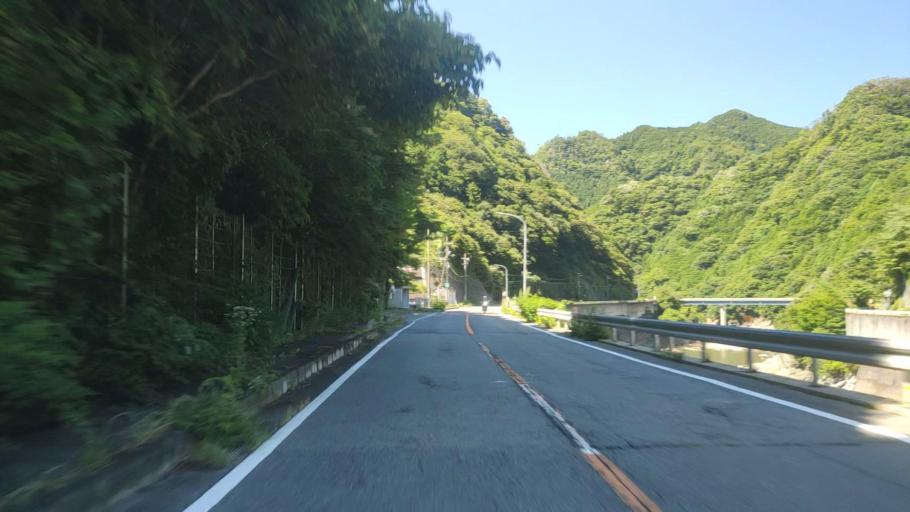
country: JP
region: Nara
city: Yoshino-cho
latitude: 34.3059
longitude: 135.9919
